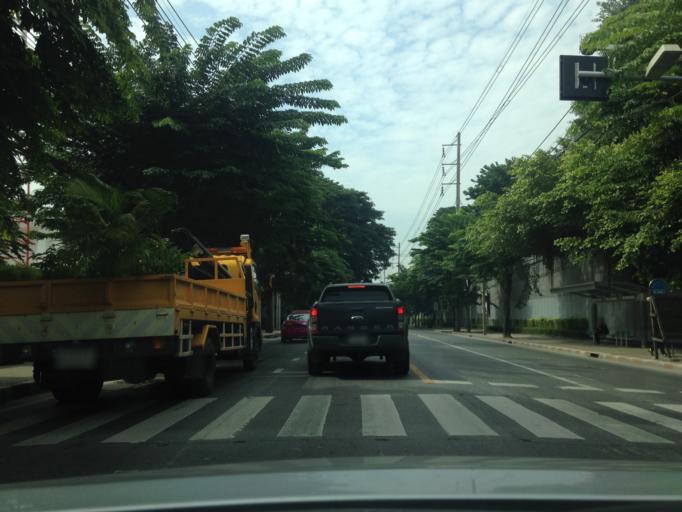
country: TH
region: Bangkok
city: Bang Phlat
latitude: 13.7953
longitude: 100.5196
